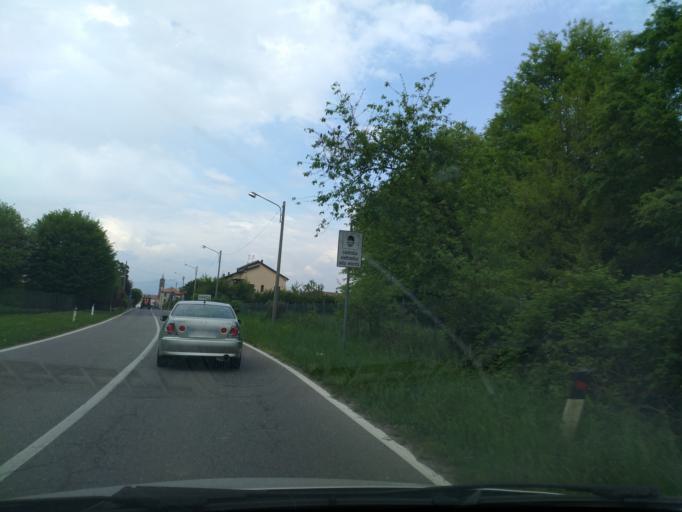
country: IT
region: Lombardy
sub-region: Provincia di Como
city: Figino Serenza
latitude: 45.7183
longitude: 9.1456
